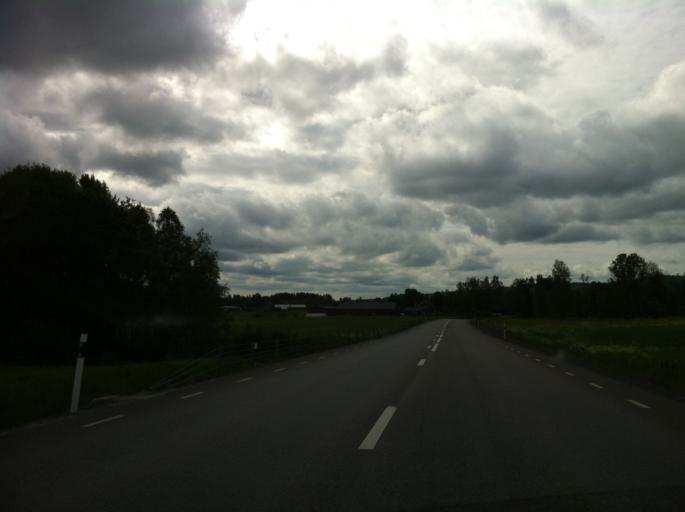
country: SE
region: Vaermland
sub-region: Sunne Kommun
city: Sunne
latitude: 59.7945
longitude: 13.1039
